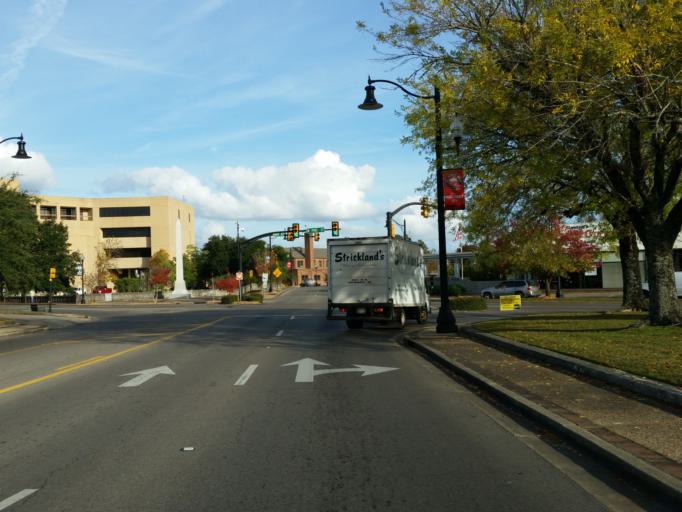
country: US
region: Mississippi
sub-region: Forrest County
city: Hattiesburg
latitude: 31.3247
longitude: -89.2934
